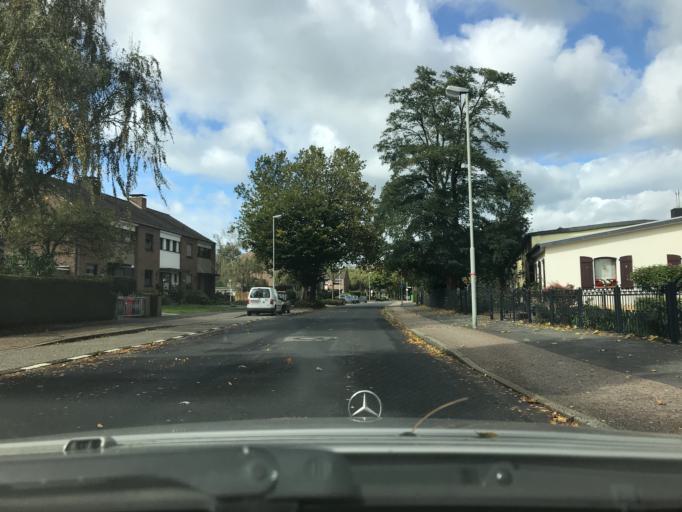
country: DE
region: North Rhine-Westphalia
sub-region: Regierungsbezirk Dusseldorf
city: Krefeld
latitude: 51.3505
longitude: 6.5564
